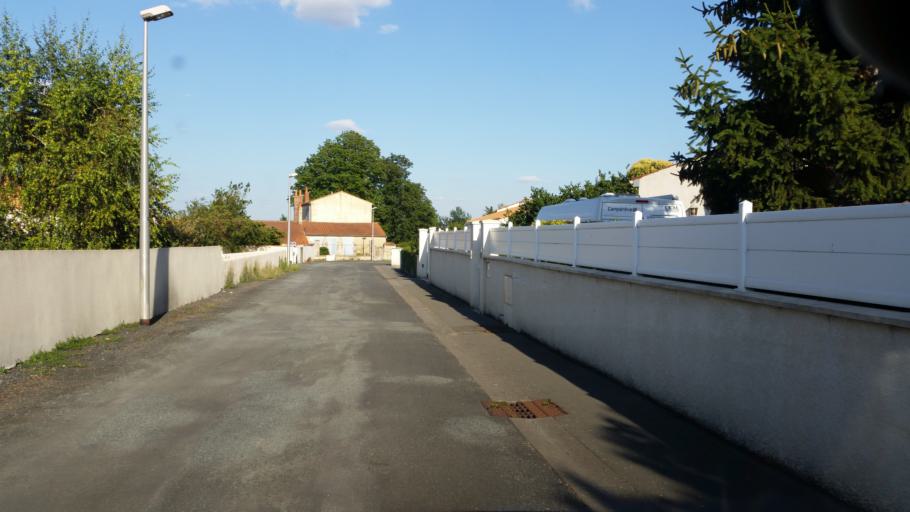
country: FR
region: Poitou-Charentes
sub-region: Departement de la Charente-Maritime
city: Marans
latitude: 46.3088
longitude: -0.9867
